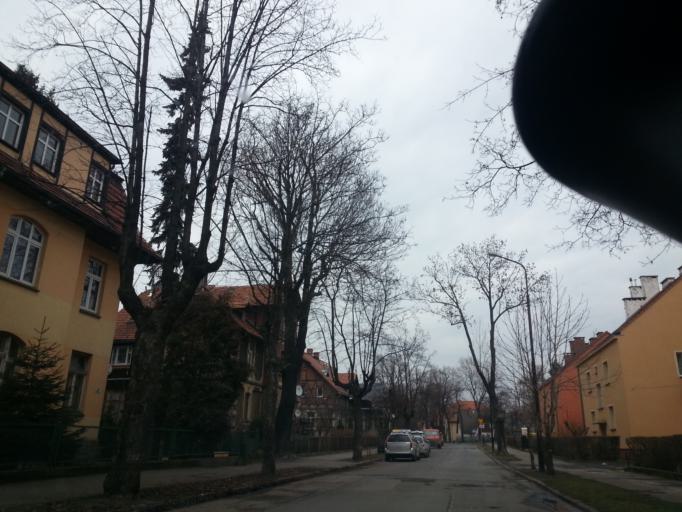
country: PL
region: Lower Silesian Voivodeship
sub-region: Jelenia Gora
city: Jelenia Gora
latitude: 50.8924
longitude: 15.7269
